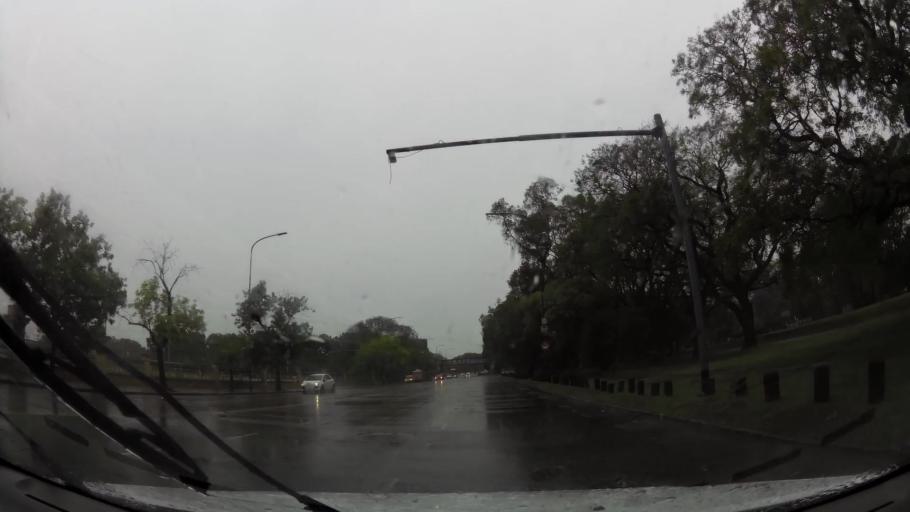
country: AR
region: Buenos Aires F.D.
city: Colegiales
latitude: -34.5677
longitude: -58.4212
